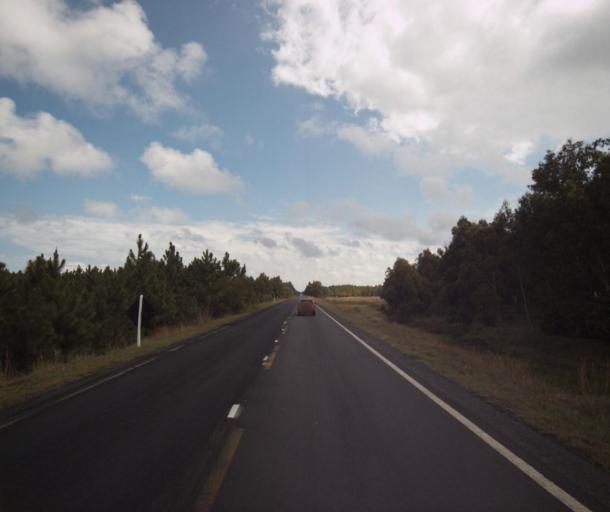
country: BR
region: Rio Grande do Sul
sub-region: Tapes
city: Tapes
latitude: -31.4123
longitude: -51.1704
